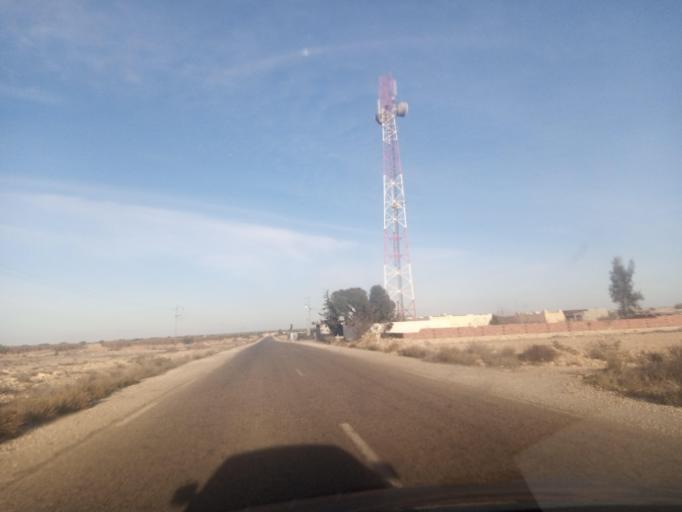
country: TN
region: Safaqis
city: Bi'r `Ali Bin Khalifah
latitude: 34.9435
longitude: 10.3475
